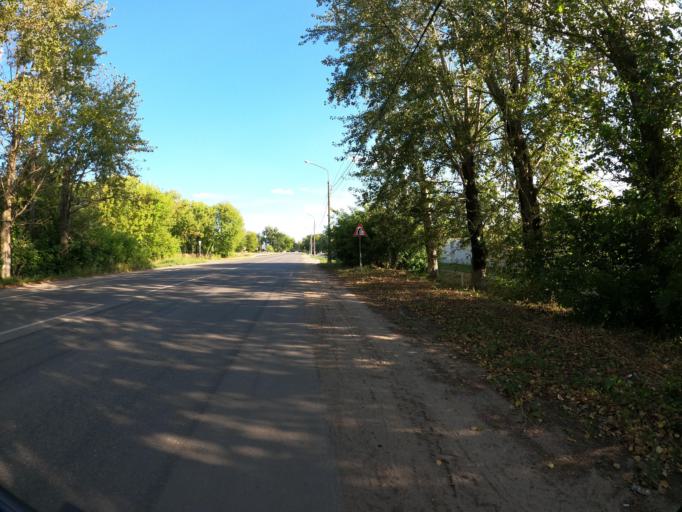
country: RU
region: Moskovskaya
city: Raduzhnyy
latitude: 55.1420
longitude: 38.7316
